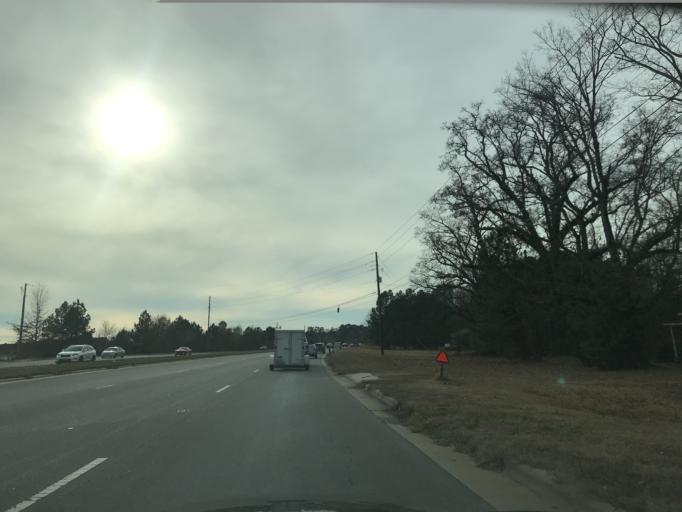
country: US
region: North Carolina
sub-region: Wake County
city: Rolesville
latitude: 35.8799
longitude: -78.5332
